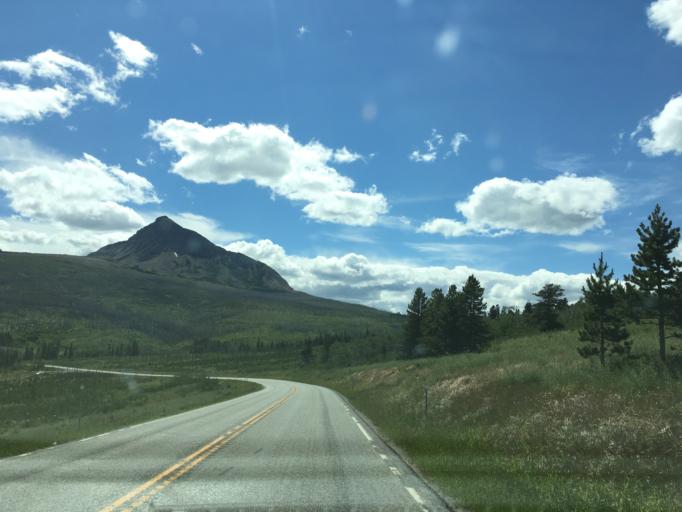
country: US
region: Montana
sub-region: Glacier County
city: North Browning
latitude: 48.6861
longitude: -113.3529
